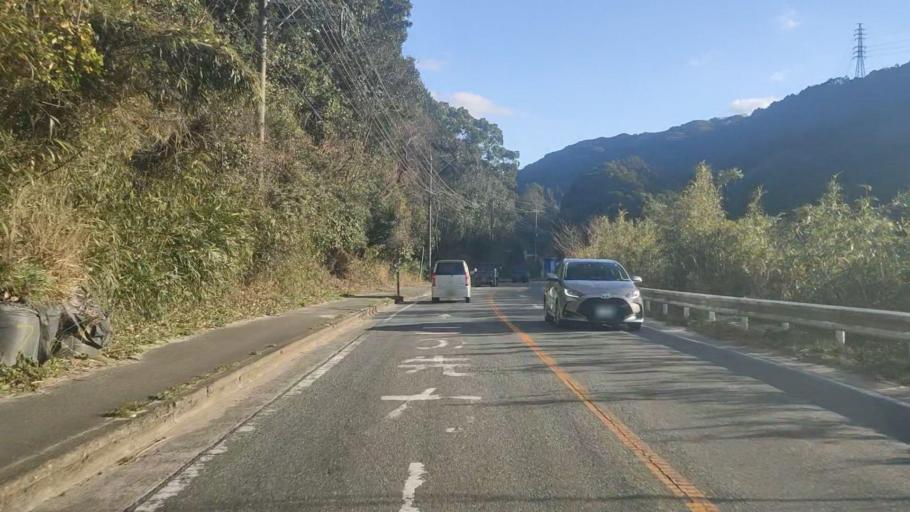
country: JP
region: Saga Prefecture
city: Saga-shi
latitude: 33.3350
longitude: 130.2620
